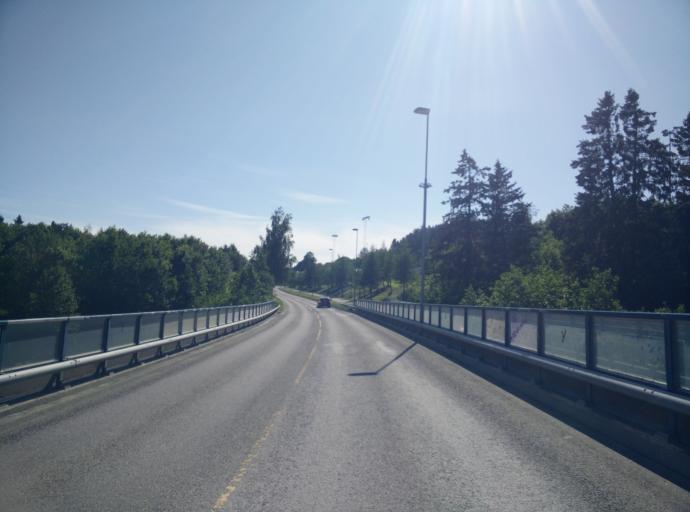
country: NO
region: Sor-Trondelag
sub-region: Trondheim
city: Trondheim
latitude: 63.3951
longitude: 10.3512
